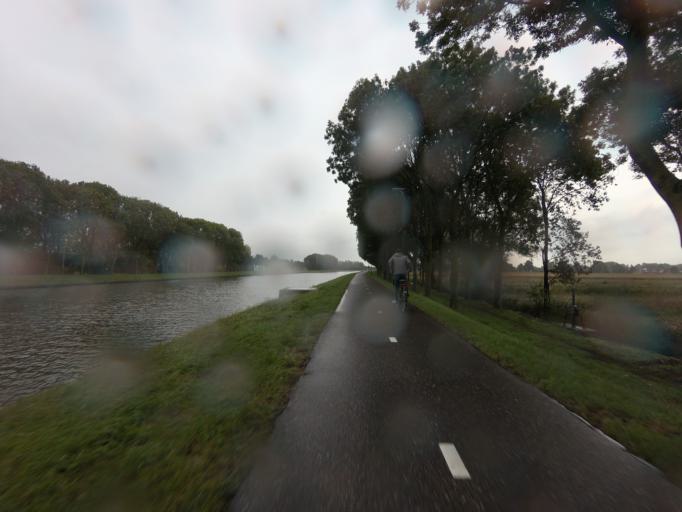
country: NL
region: South Holland
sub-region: Gemeente Gorinchem
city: Gorinchem
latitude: 51.8574
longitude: 4.9838
